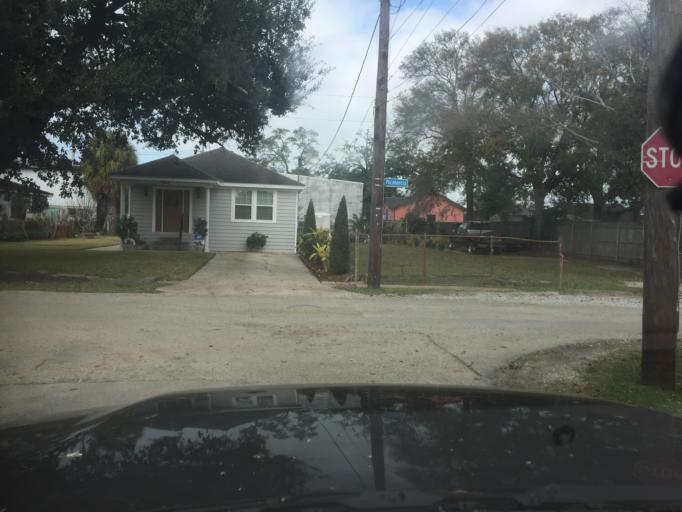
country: US
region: Louisiana
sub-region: Orleans Parish
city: New Orleans
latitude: 30.0016
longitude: -90.0426
